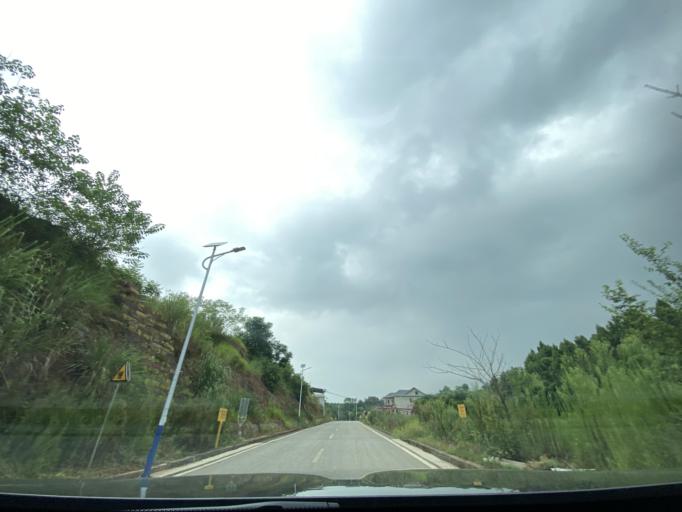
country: CN
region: Sichuan
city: Jiancheng
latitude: 30.5443
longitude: 104.5193
